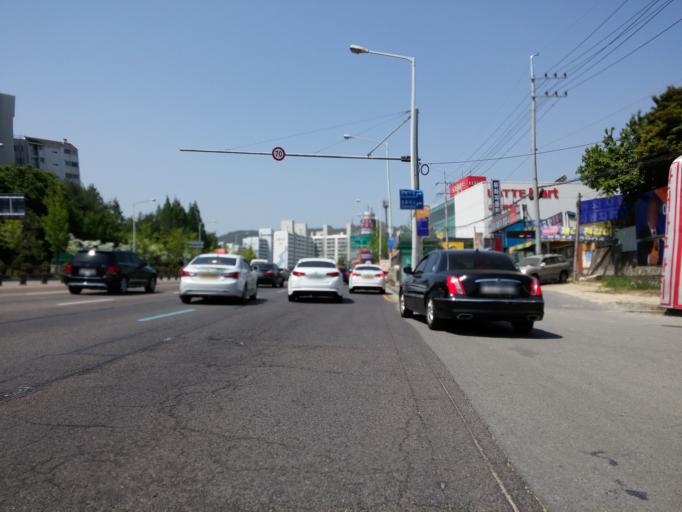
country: KR
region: Daejeon
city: Daejeon
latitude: 36.3007
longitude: 127.3267
